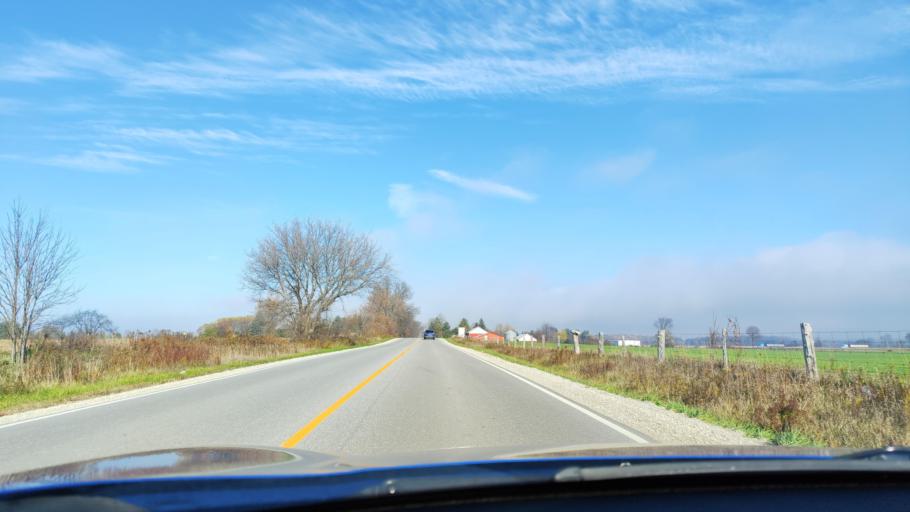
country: CA
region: Ontario
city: Wasaga Beach
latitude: 44.4177
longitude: -80.0618
